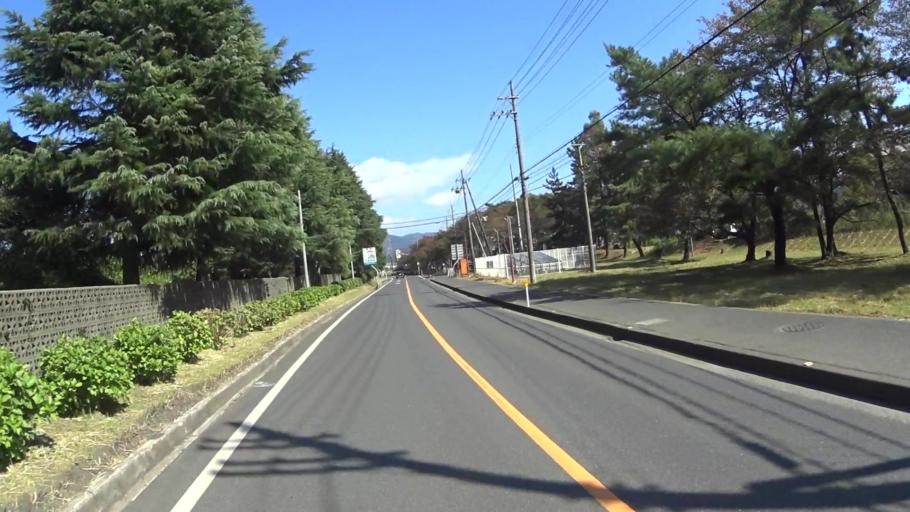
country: JP
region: Kyoto
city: Miyazu
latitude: 35.5561
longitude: 135.1516
